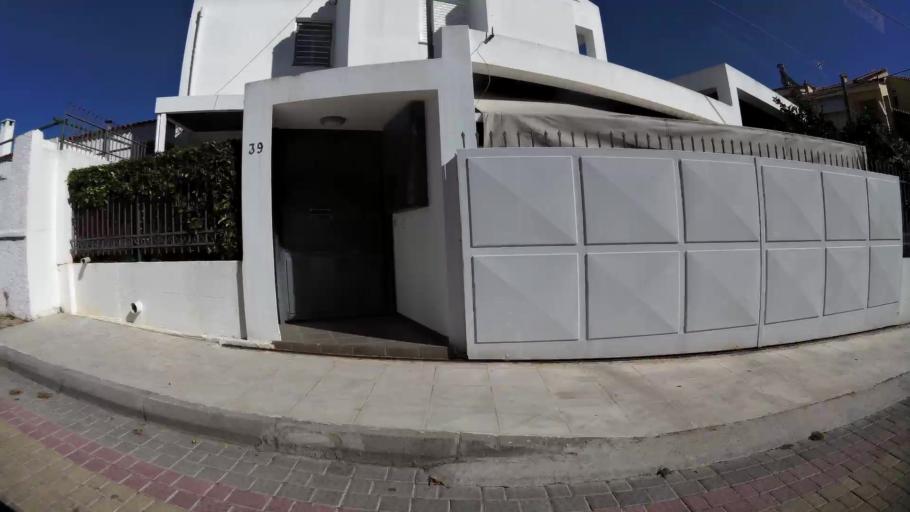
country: GR
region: Attica
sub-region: Nomarchia Anatolikis Attikis
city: Gerakas
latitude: 38.0070
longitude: 23.8511
